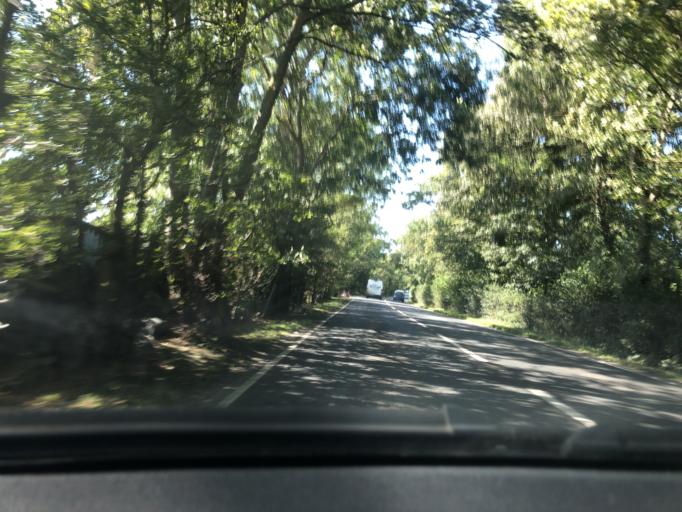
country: GB
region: England
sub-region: Somerset
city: Woolavington
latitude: 51.1542
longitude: -2.9260
